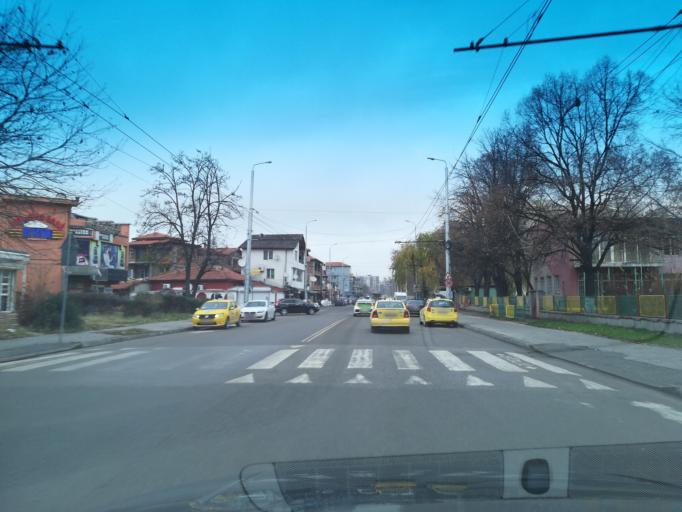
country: BG
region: Plovdiv
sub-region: Obshtina Plovdiv
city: Plovdiv
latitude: 42.1504
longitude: 24.7867
